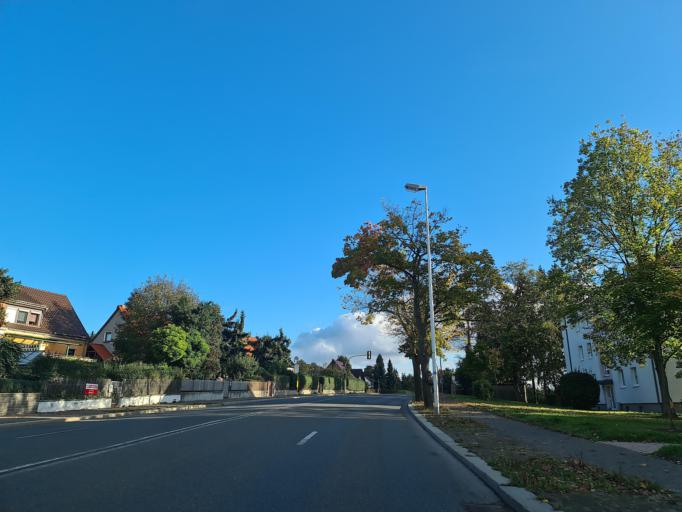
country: DE
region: Thuringia
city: Gera
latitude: 50.8837
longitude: 12.0994
